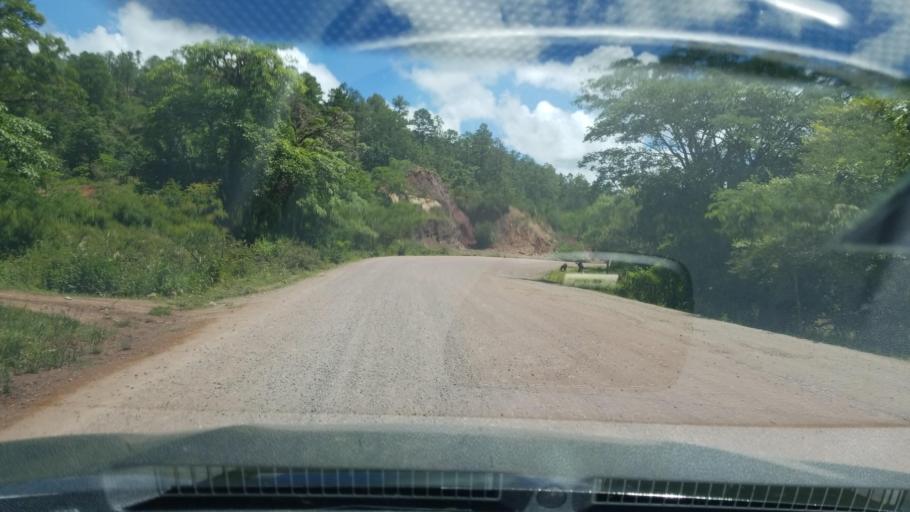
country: HN
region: Francisco Morazan
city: Talanga
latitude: 14.3398
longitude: -87.0432
